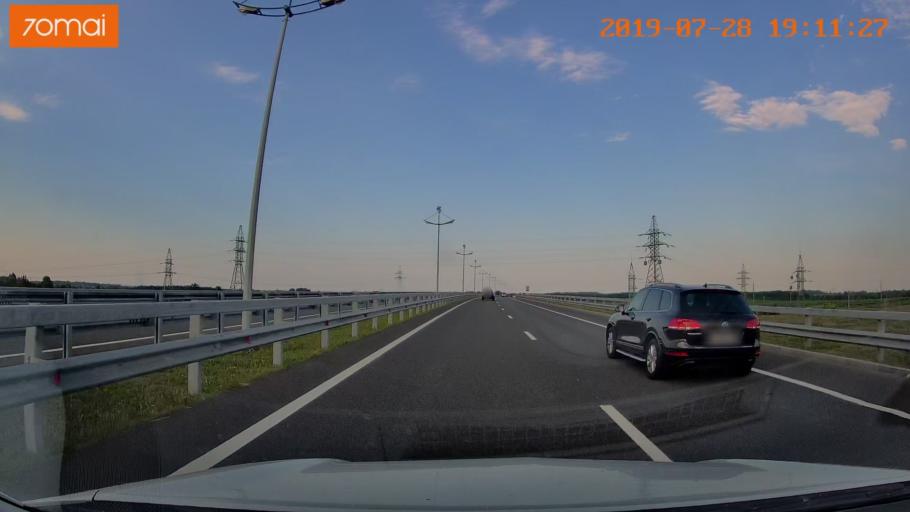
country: RU
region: Kaliningrad
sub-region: Gorod Kaliningrad
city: Pionerskiy
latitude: 54.9144
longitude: 20.2303
